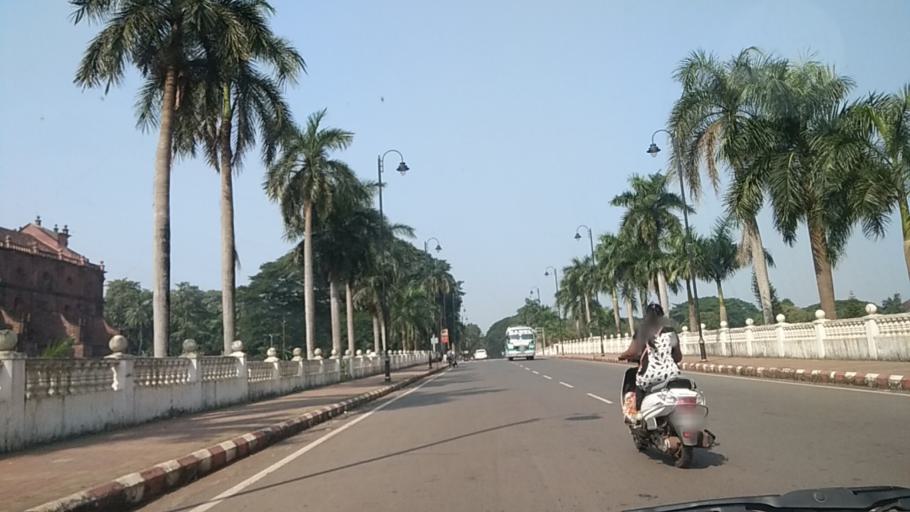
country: IN
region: Goa
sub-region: North Goa
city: Jua
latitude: 15.5014
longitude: 73.9126
